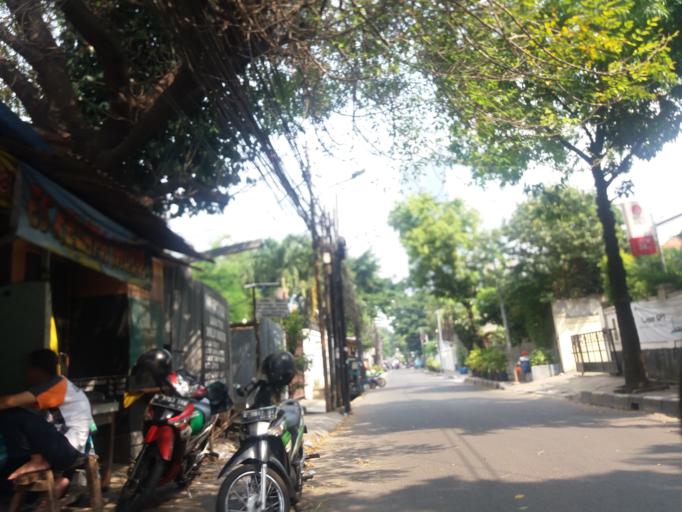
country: ID
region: Jakarta Raya
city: Jakarta
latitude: -6.2257
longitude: 106.8215
